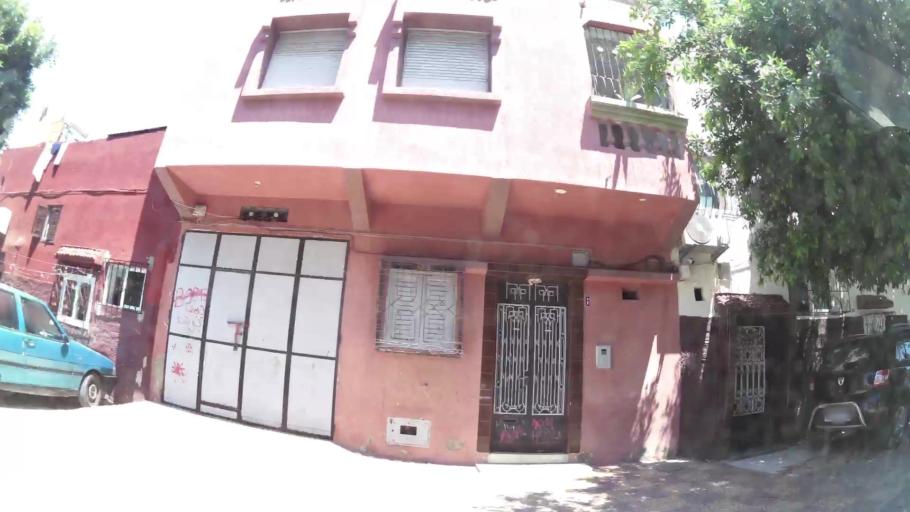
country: MA
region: Gharb-Chrarda-Beni Hssen
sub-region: Kenitra Province
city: Kenitra
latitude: 34.2585
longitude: -6.5614
